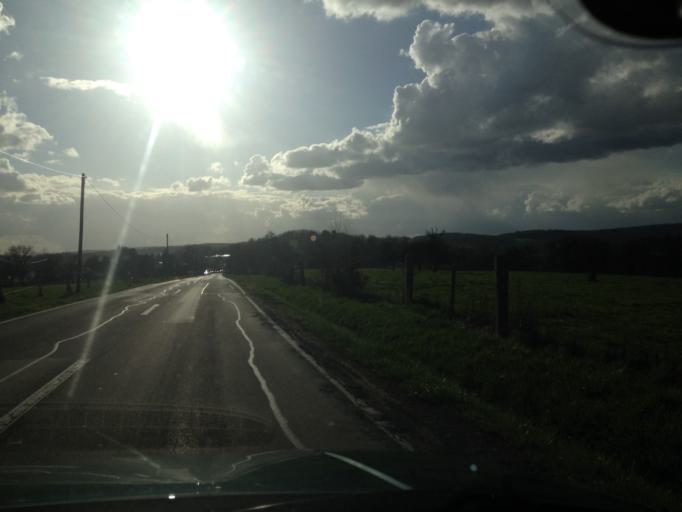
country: DE
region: Saarland
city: Mainzweiler
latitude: 49.4010
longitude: 7.1055
